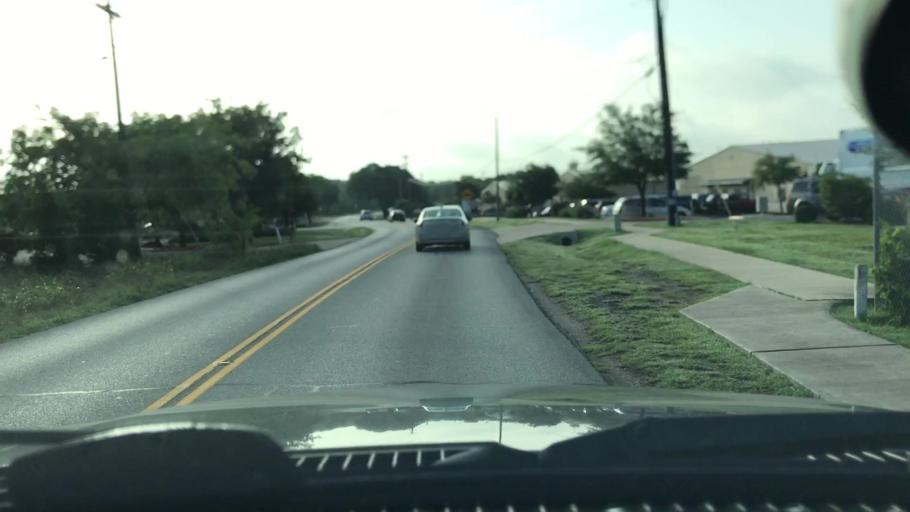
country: US
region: Texas
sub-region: Williamson County
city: Cedar Park
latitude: 30.5050
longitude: -97.8153
